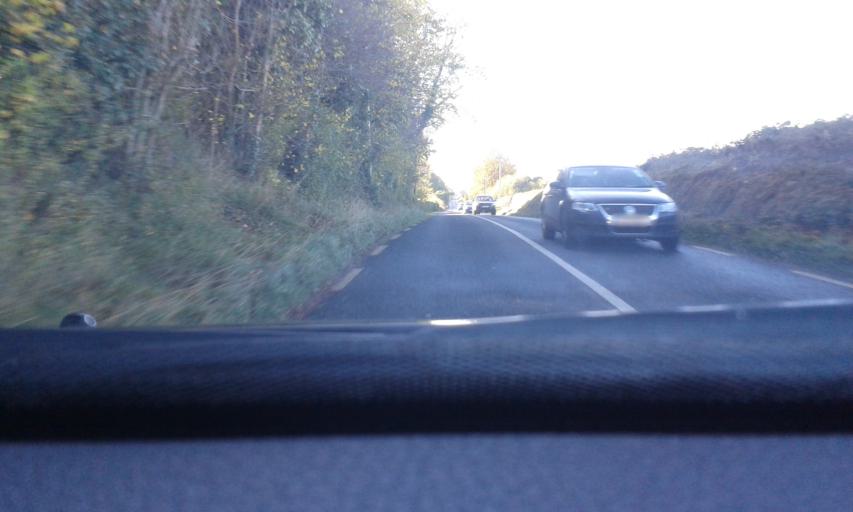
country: IE
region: Leinster
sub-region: Kildare
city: Rathangan
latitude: 53.1890
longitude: -7.0130
